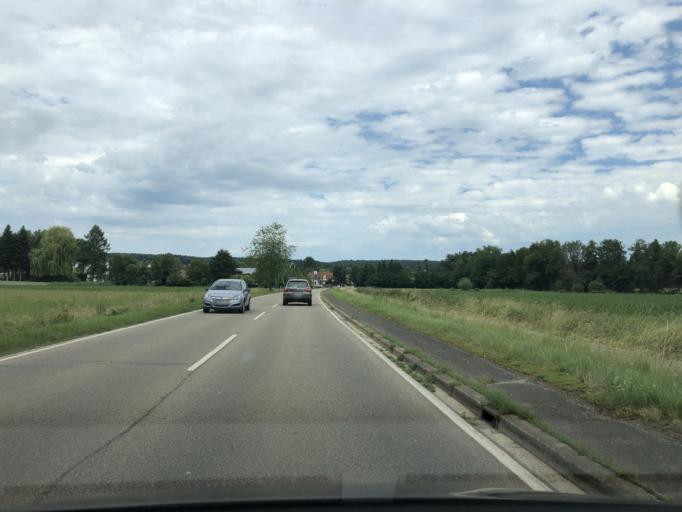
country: DE
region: Baden-Wuerttemberg
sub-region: Karlsruhe Region
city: Aglasterhausen
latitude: 49.3641
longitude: 8.9818
